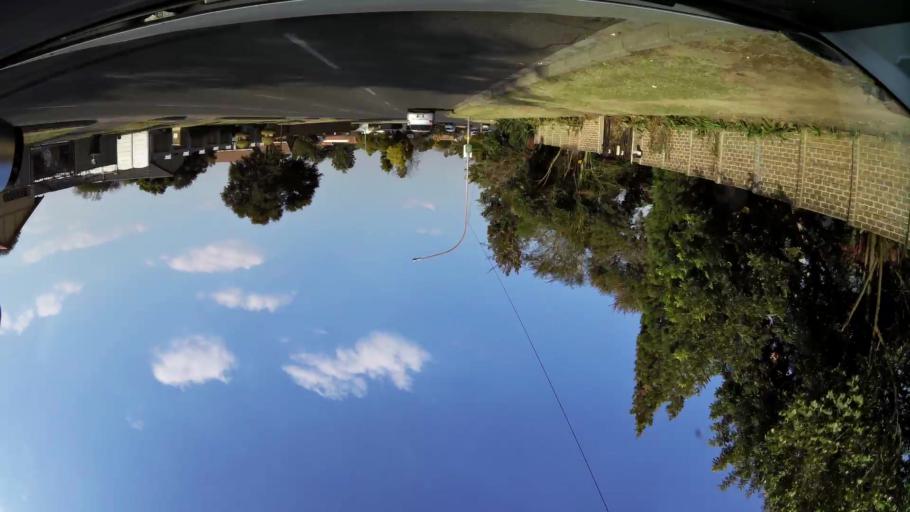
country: ZA
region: Gauteng
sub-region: City of Johannesburg Metropolitan Municipality
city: Modderfontein
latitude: -26.0741
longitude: 28.2092
